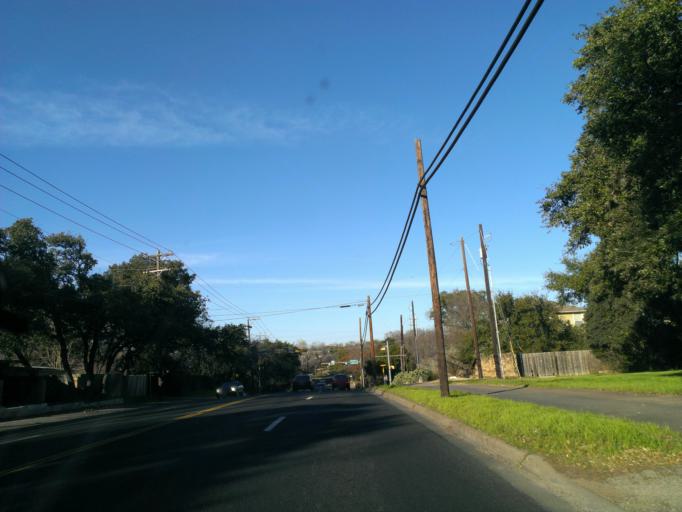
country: US
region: Texas
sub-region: Travis County
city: Rollingwood
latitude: 30.2200
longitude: -97.7945
